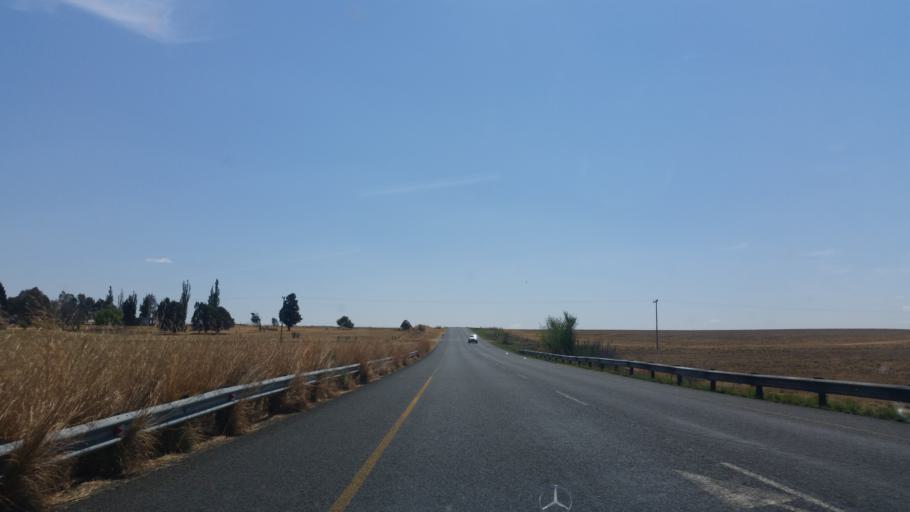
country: ZA
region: Orange Free State
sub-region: Thabo Mofutsanyana District Municipality
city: Phuthaditjhaba
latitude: -28.1923
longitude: 28.6867
